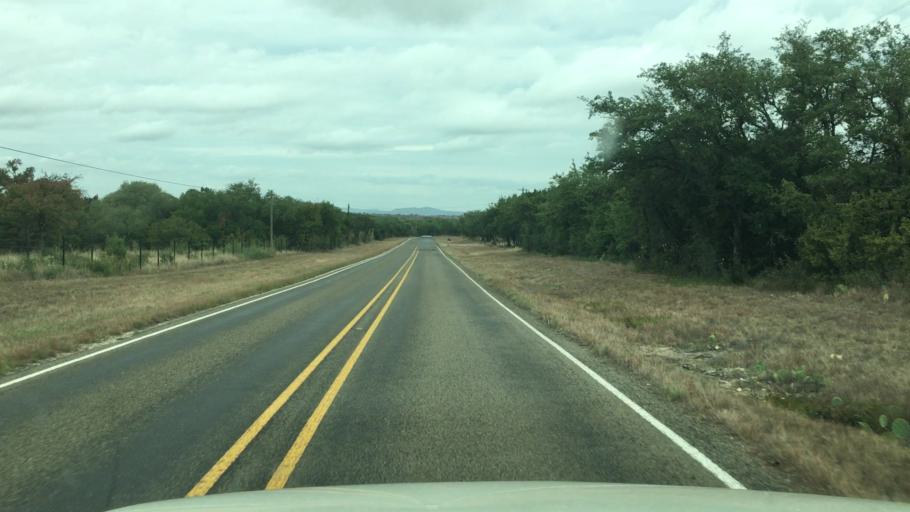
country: US
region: Texas
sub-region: Llano County
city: Horseshoe Bay
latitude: 30.4701
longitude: -98.4140
